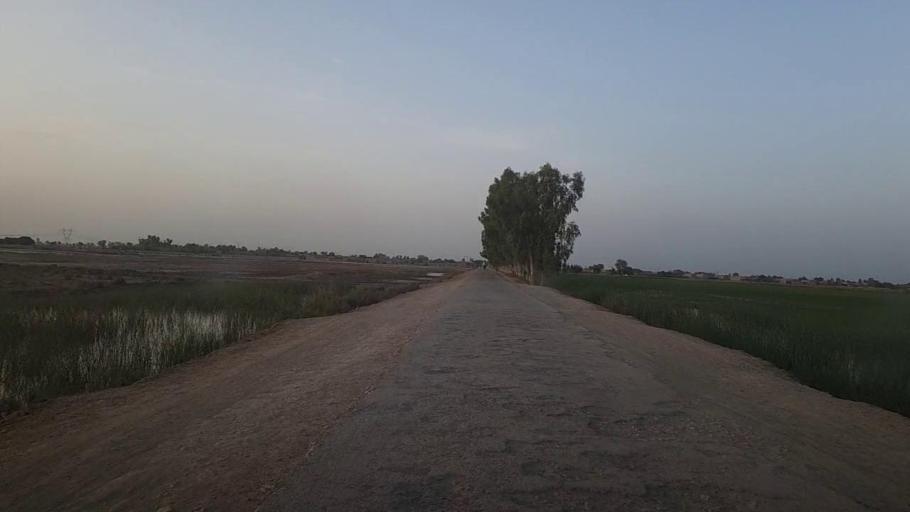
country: PK
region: Sindh
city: Radhan
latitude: 27.1272
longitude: 67.9289
